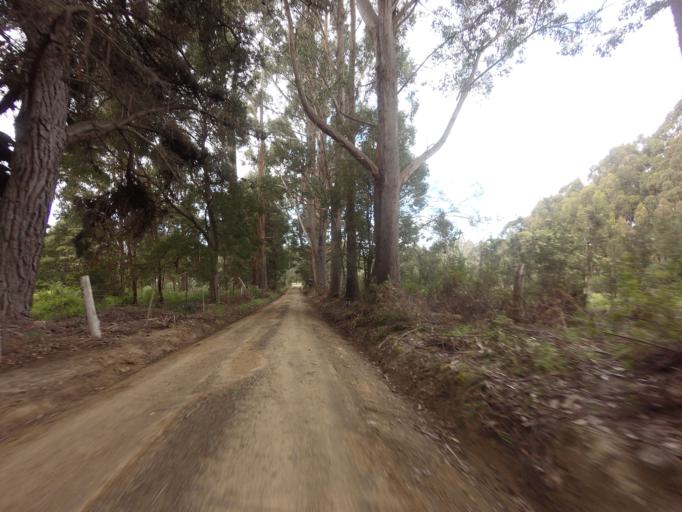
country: AU
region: Tasmania
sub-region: Huon Valley
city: Geeveston
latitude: -43.4053
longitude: 147.0128
